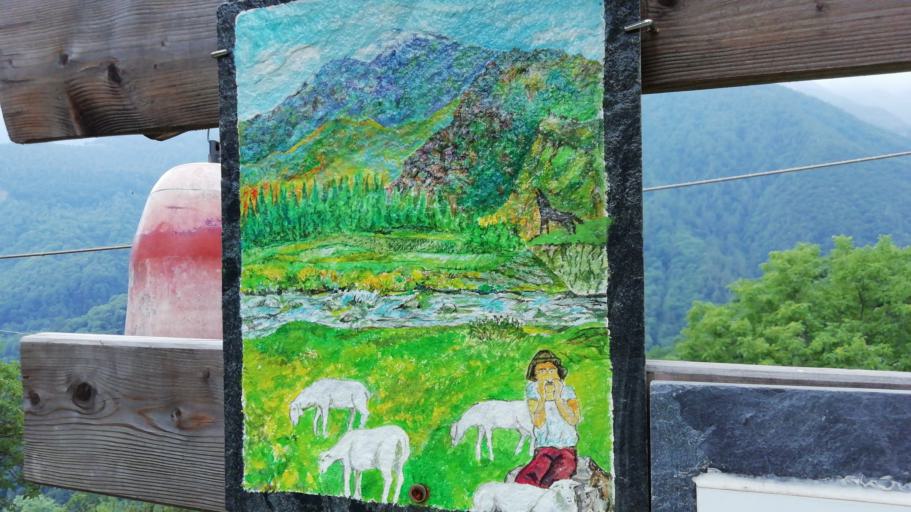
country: IT
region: Piedmont
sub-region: Provincia Verbano-Cusio-Ossola
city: San Lorenzo
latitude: 46.1261
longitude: 8.2035
